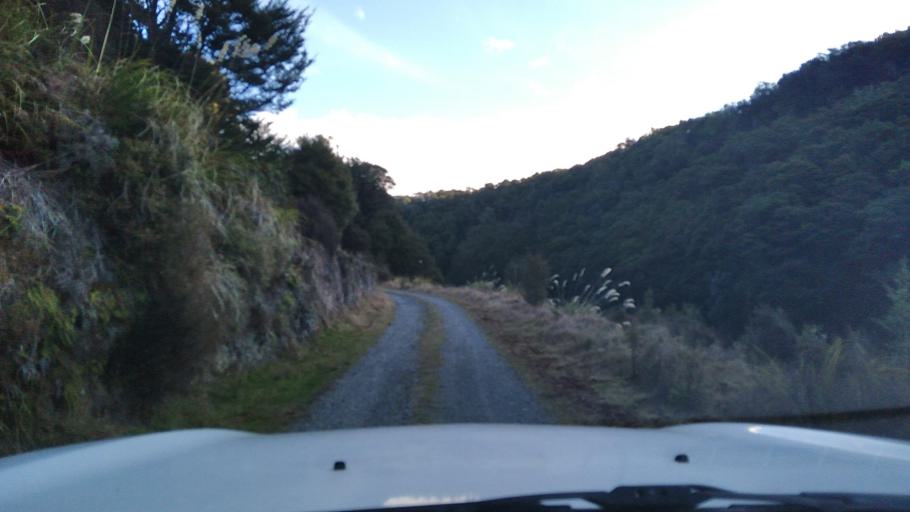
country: NZ
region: Waikato
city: Turangi
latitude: -39.2122
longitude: 175.7769
